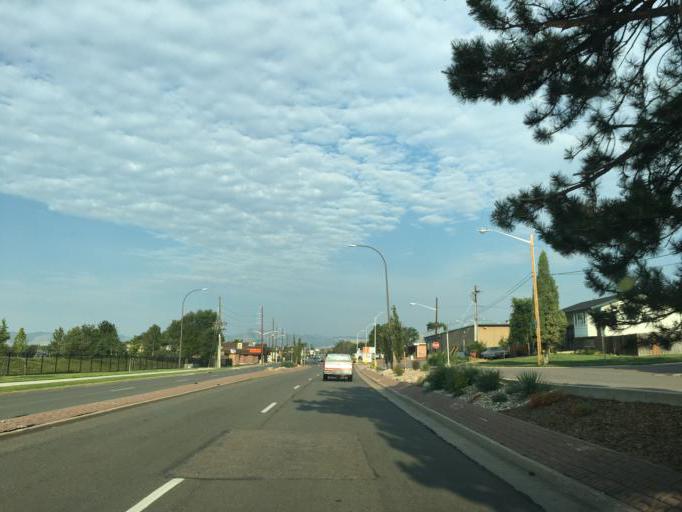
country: US
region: Colorado
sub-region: Jefferson County
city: Lakewood
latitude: 39.6822
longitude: -105.0776
